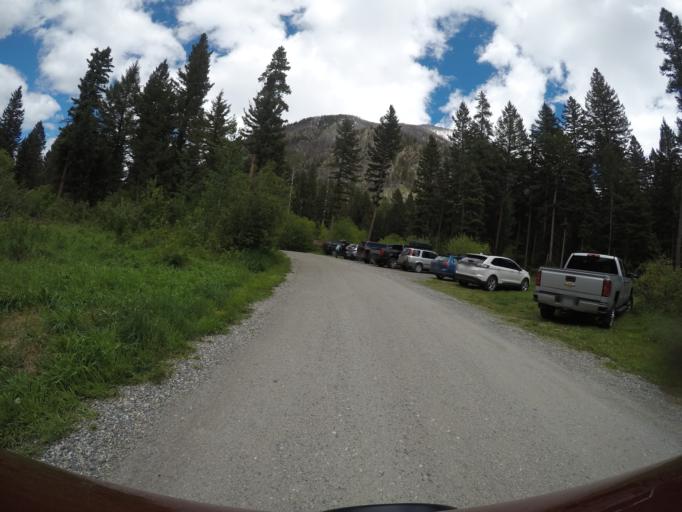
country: US
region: Montana
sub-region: Park County
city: Livingston
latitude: 45.4974
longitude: -110.5200
